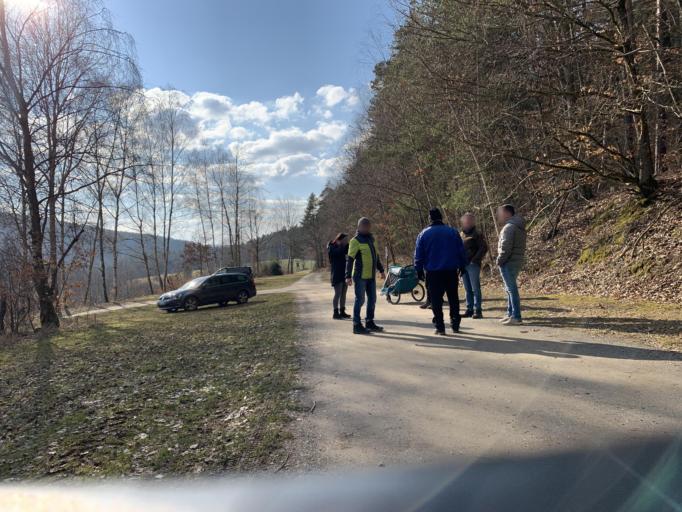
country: DE
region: Bavaria
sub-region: Upper Palatinate
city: Thanstein
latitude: 49.3773
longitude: 12.4339
